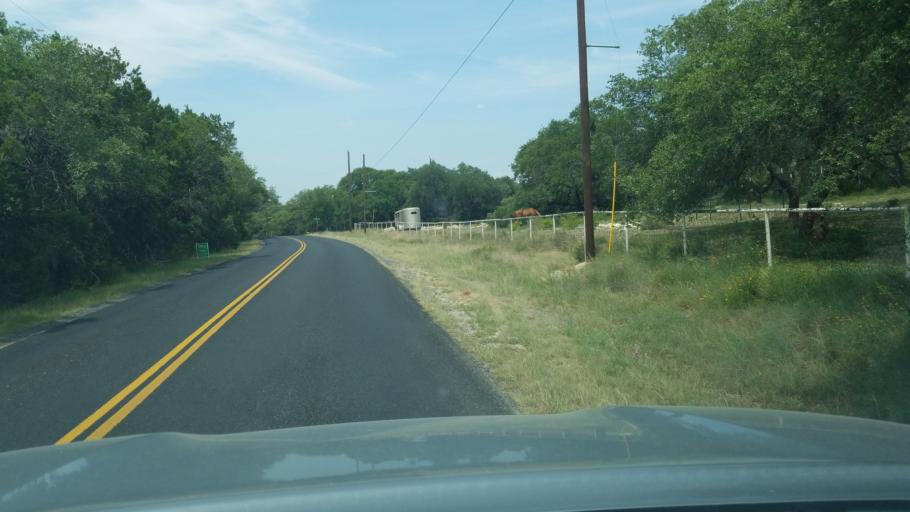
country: US
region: Texas
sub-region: Comal County
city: Bulverde
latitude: 29.7737
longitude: -98.4466
